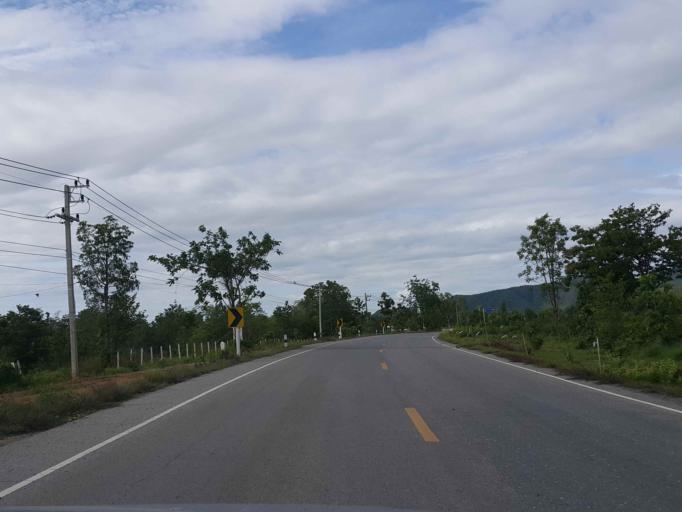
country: TH
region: Sukhothai
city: Thung Saliam
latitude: 17.2364
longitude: 99.5153
